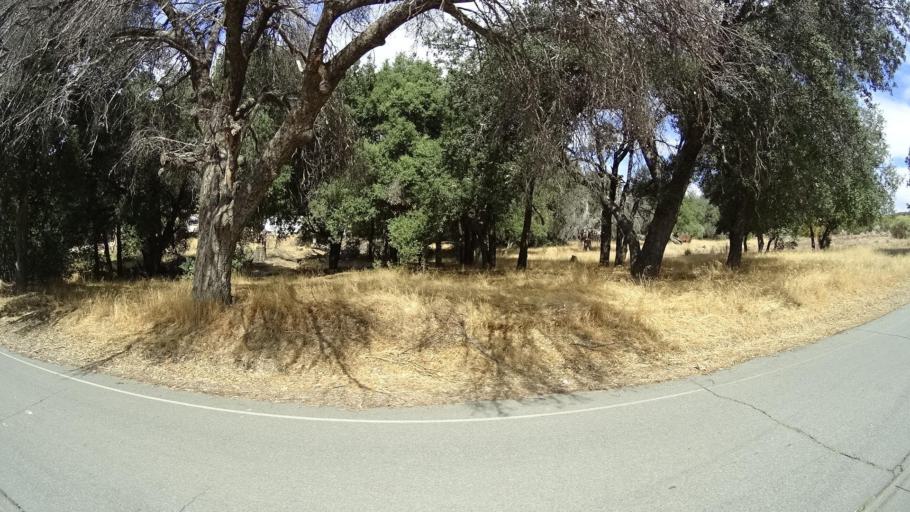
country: US
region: California
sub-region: San Diego County
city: Campo
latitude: 32.6930
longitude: -116.3332
